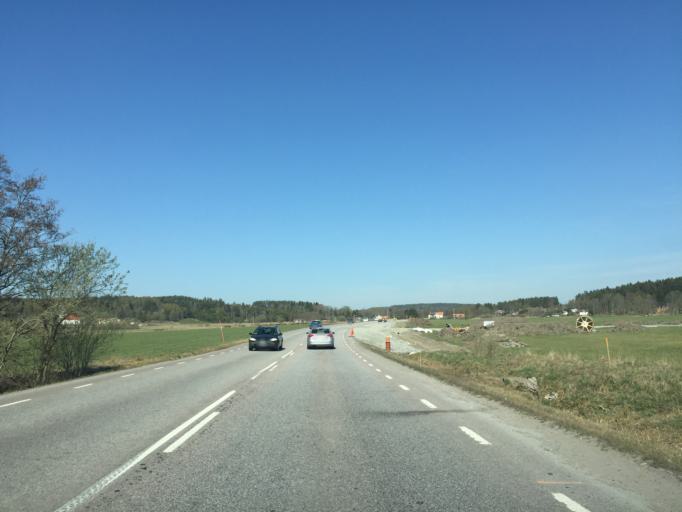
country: SE
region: Vaestra Goetaland
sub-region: Kungalvs Kommun
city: Kungalv
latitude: 57.9060
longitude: 11.9235
